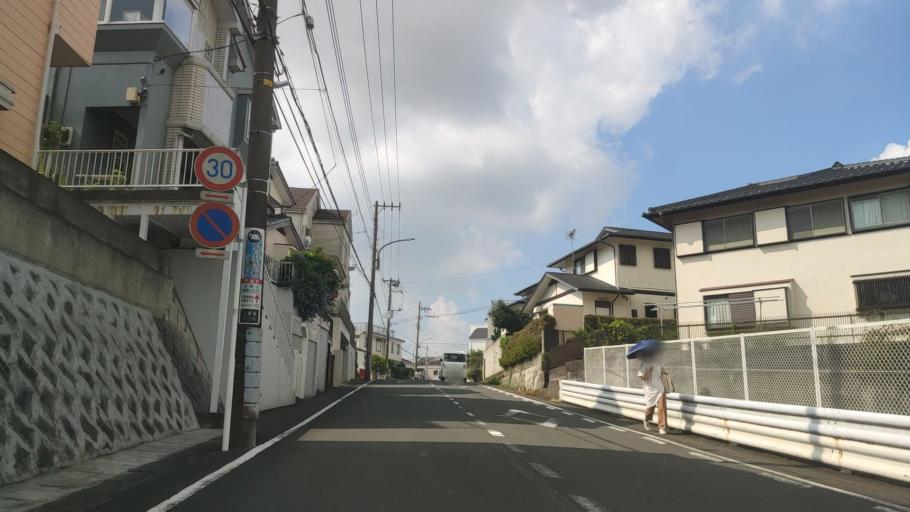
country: JP
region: Kanagawa
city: Yokohama
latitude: 35.4014
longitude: 139.5647
